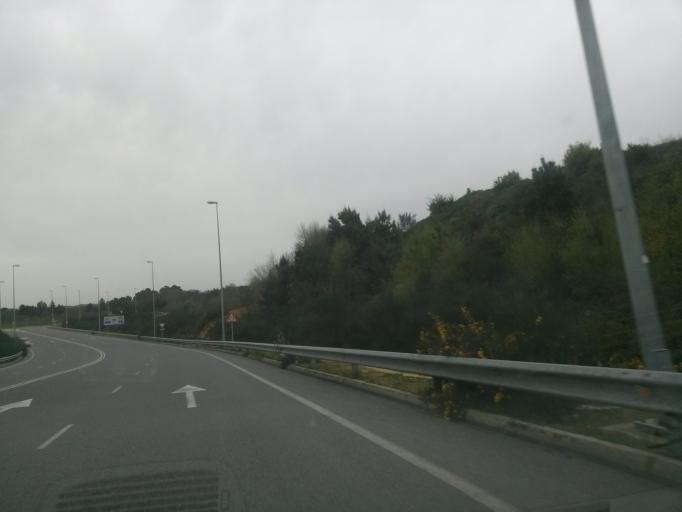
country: ES
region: Galicia
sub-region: Provincia de Lugo
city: Lugo
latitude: 43.0239
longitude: -7.5339
